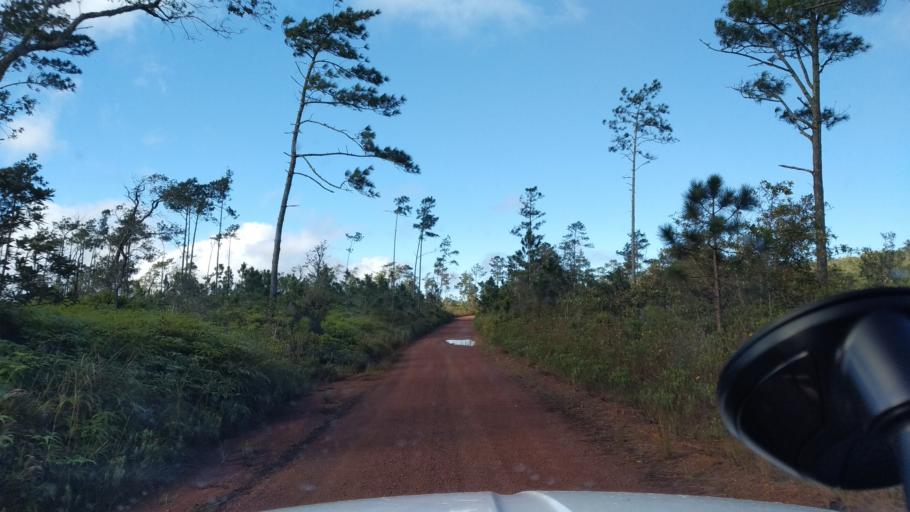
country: BZ
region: Cayo
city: Belmopan
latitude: 16.9983
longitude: -88.8415
